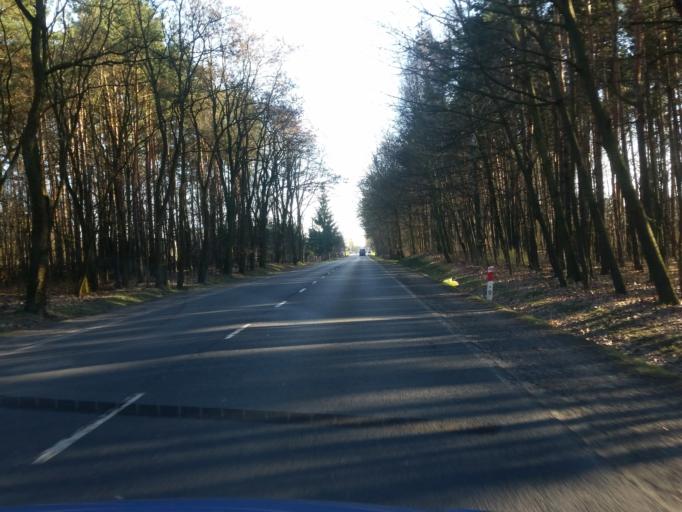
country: PL
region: Lodz Voivodeship
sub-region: Powiat radomszczanski
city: Gomunice
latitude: 51.1654
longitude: 19.4925
